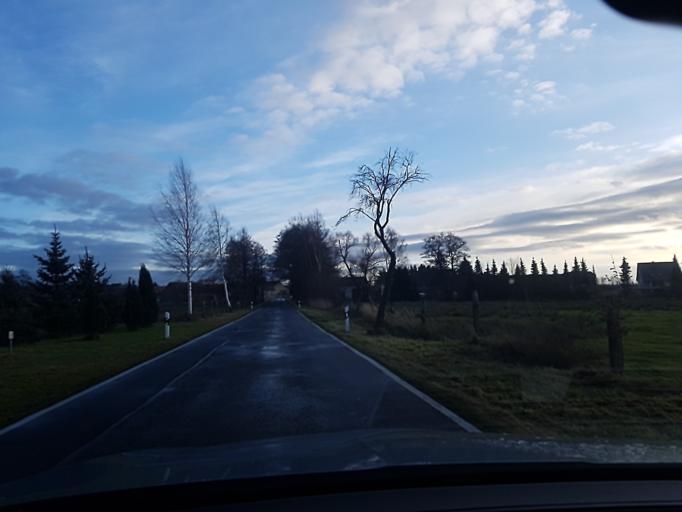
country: DE
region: Brandenburg
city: Schilda
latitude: 51.5774
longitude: 13.4049
